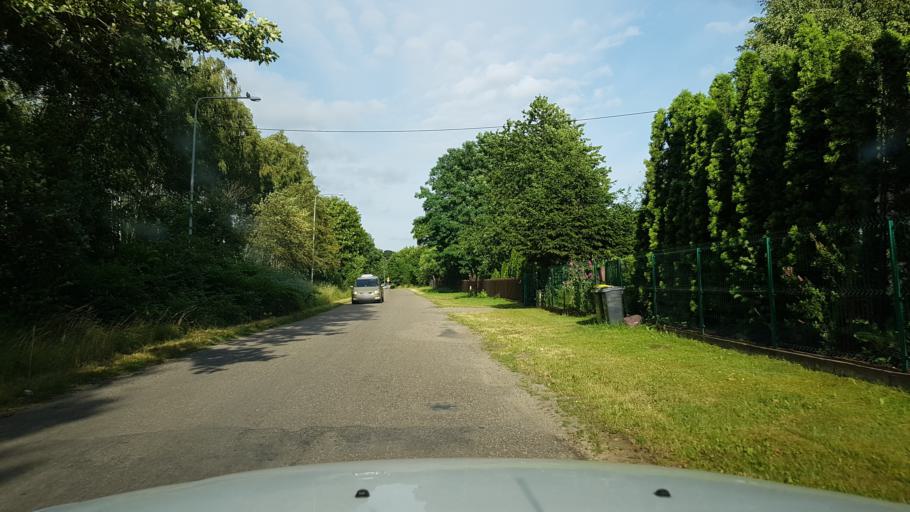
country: PL
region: West Pomeranian Voivodeship
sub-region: Powiat kolobrzeski
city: Kolobrzeg
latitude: 54.0889
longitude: 15.5581
